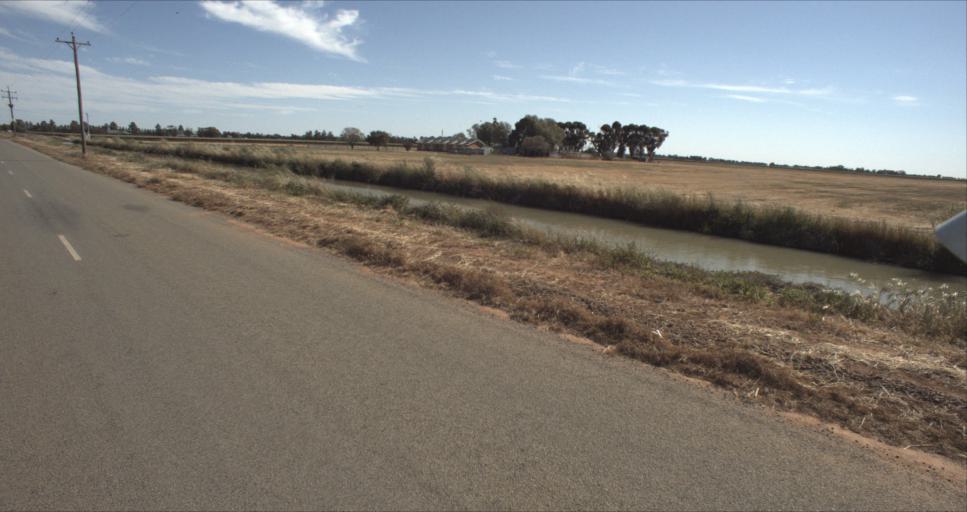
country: AU
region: New South Wales
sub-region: Leeton
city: Leeton
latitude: -34.5760
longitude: 146.3808
